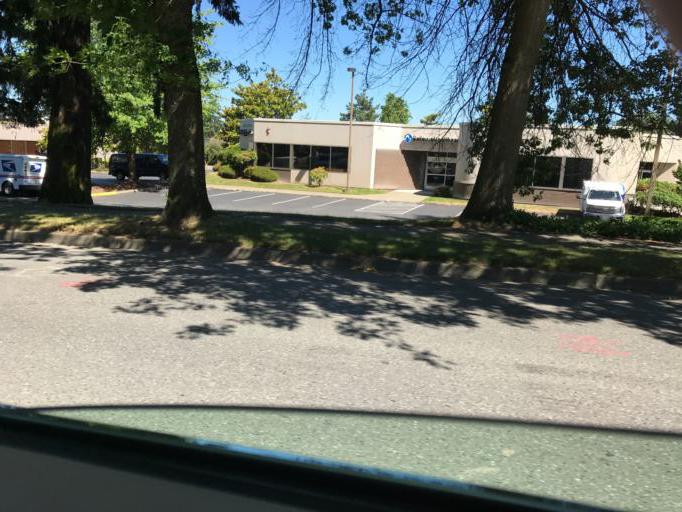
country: US
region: Washington
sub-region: King County
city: Redmond
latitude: 47.6280
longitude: -122.1382
